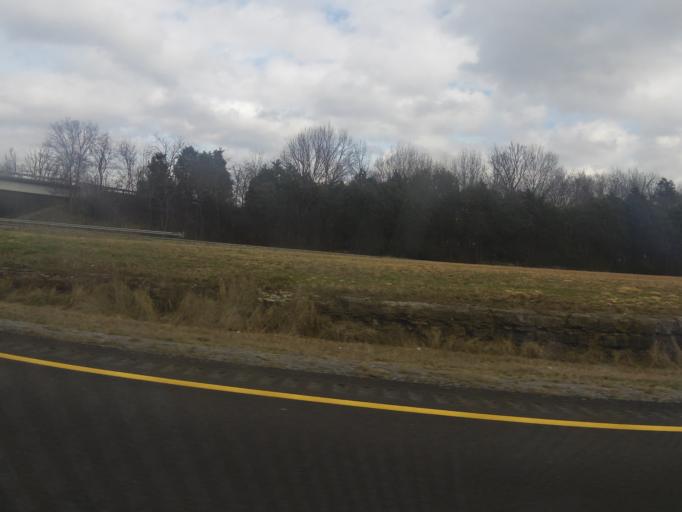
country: US
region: Tennessee
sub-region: Rutherford County
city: Plainview
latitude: 35.7453
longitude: -86.3391
